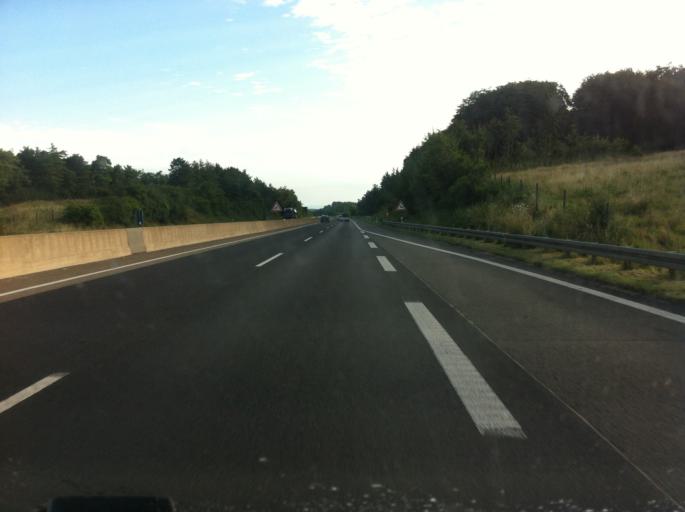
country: DE
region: North Rhine-Westphalia
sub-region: Regierungsbezirk Koln
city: Nettersheim
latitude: 50.5314
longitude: 6.6725
